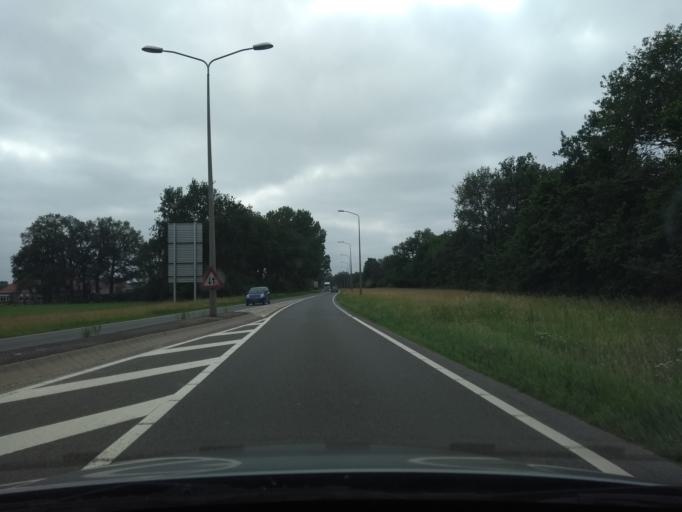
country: NL
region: Overijssel
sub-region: Gemeente Wierden
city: Wierden
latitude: 52.3500
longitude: 6.6245
